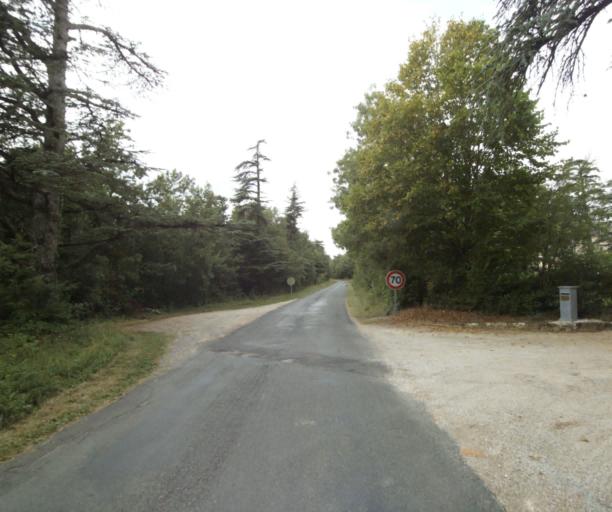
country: FR
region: Midi-Pyrenees
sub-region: Departement du Tarn
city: Soreze
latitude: 43.4656
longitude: 2.0836
